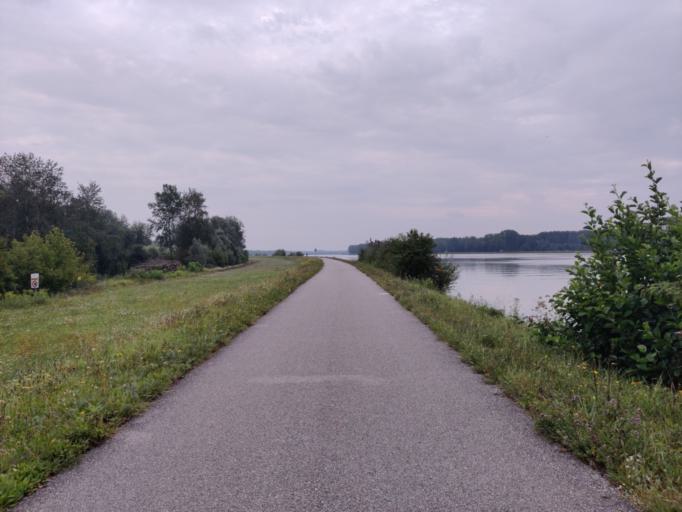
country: AT
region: Upper Austria
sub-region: Politischer Bezirk Urfahr-Umgebung
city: Steyregg
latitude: 48.2595
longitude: 14.4011
